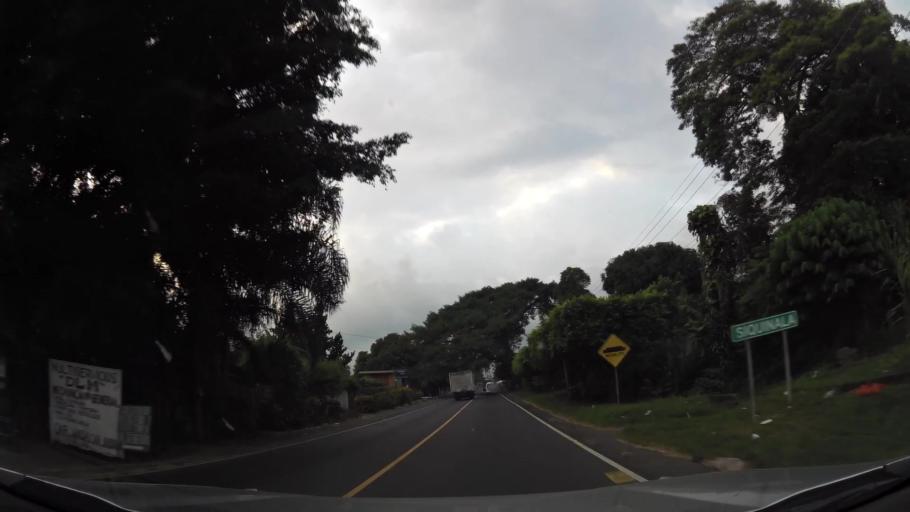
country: GT
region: Escuintla
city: Siquinala
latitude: 14.3046
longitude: -90.9616
